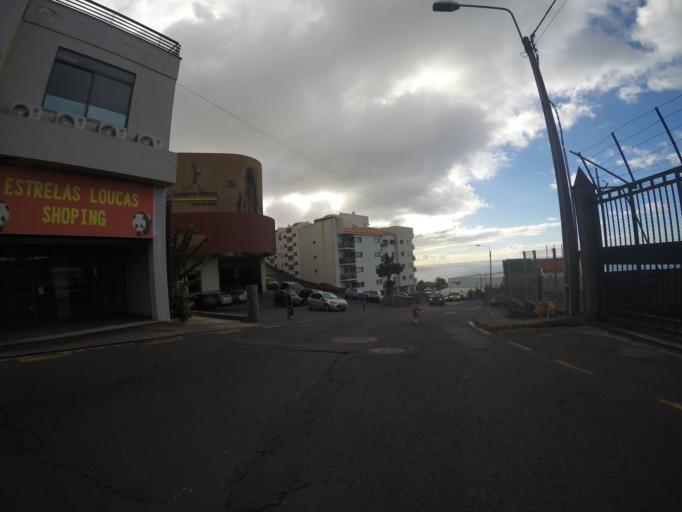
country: PT
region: Madeira
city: Canico
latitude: 32.6474
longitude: -16.8580
